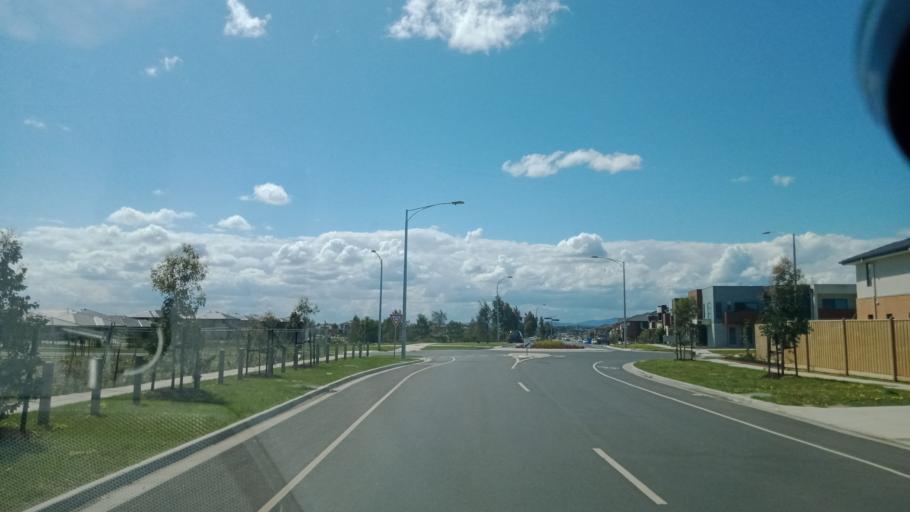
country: AU
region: Victoria
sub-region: Casey
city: Cranbourne West
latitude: -38.1020
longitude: 145.2488
